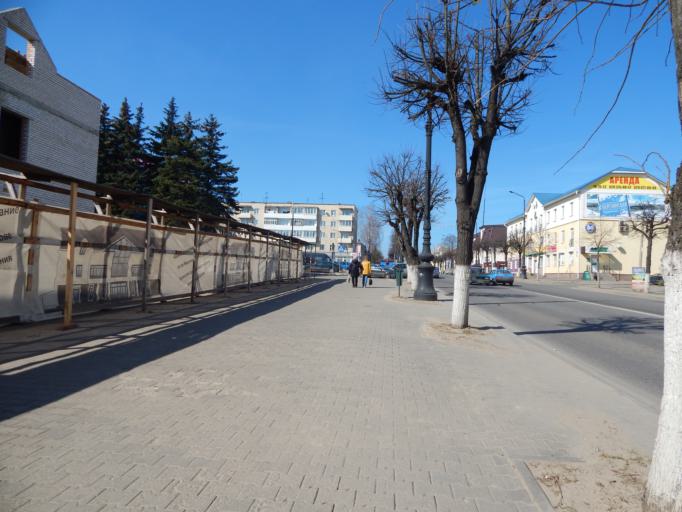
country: BY
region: Minsk
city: Horad Barysaw
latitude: 54.2216
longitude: 28.5233
